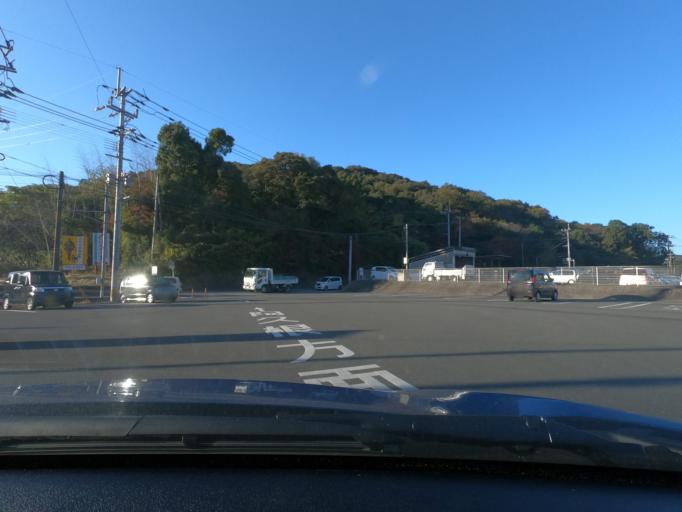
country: JP
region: Kagoshima
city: Satsumasendai
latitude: 31.8469
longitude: 130.2715
